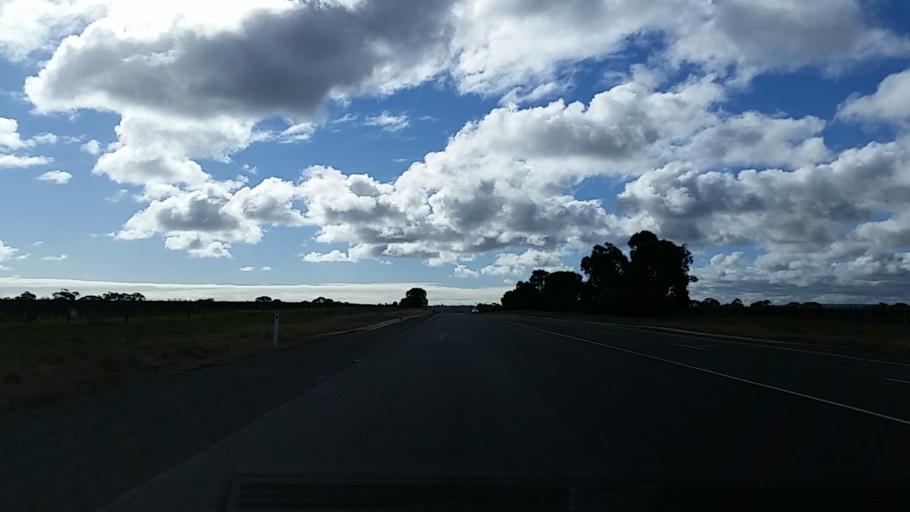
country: AU
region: South Australia
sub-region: Onkaparinga
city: McLaren Vale
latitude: -35.2355
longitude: 138.5255
